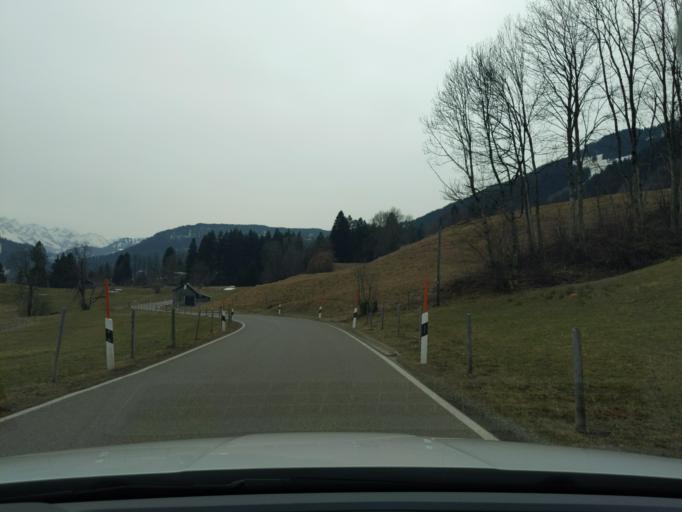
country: DE
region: Bavaria
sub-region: Swabia
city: Bolsterlang
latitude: 47.4696
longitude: 10.2304
